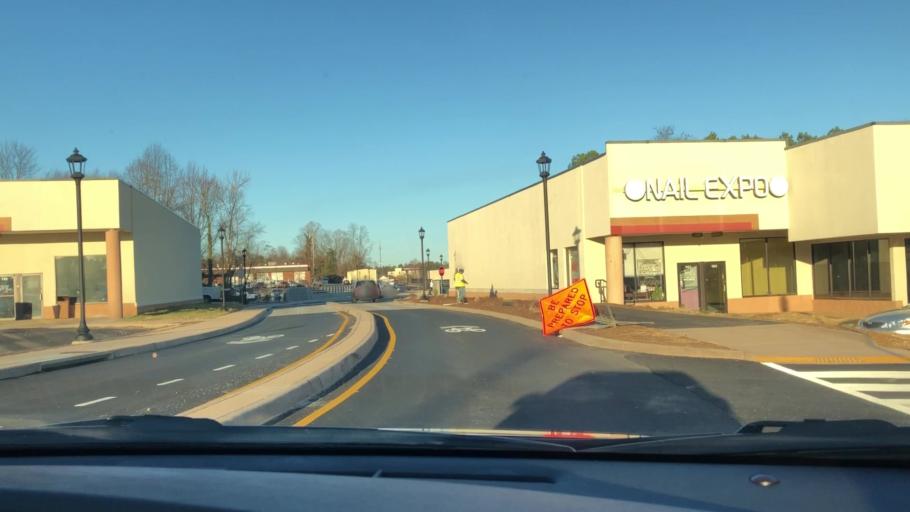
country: US
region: Virginia
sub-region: City of Charlottesville
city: Charlottesville
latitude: 38.0652
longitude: -78.4860
